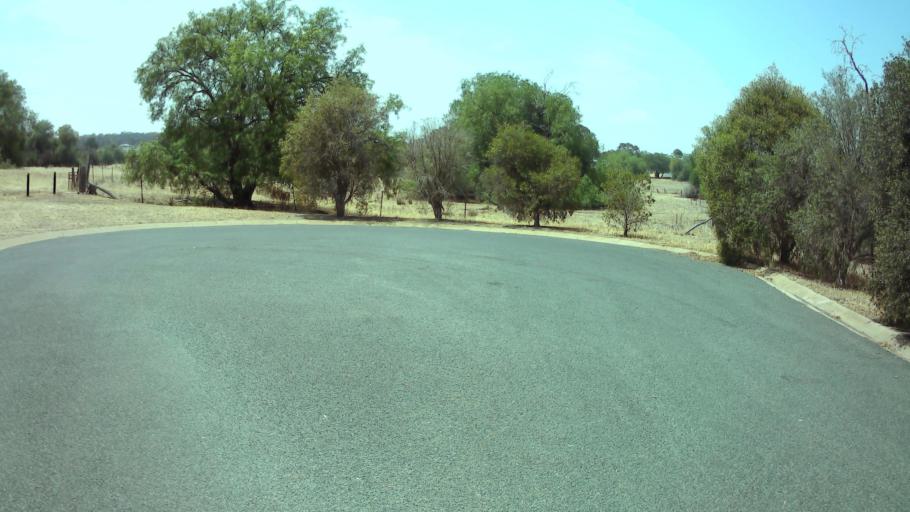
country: AU
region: New South Wales
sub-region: Weddin
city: Grenfell
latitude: -33.8977
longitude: 148.1678
